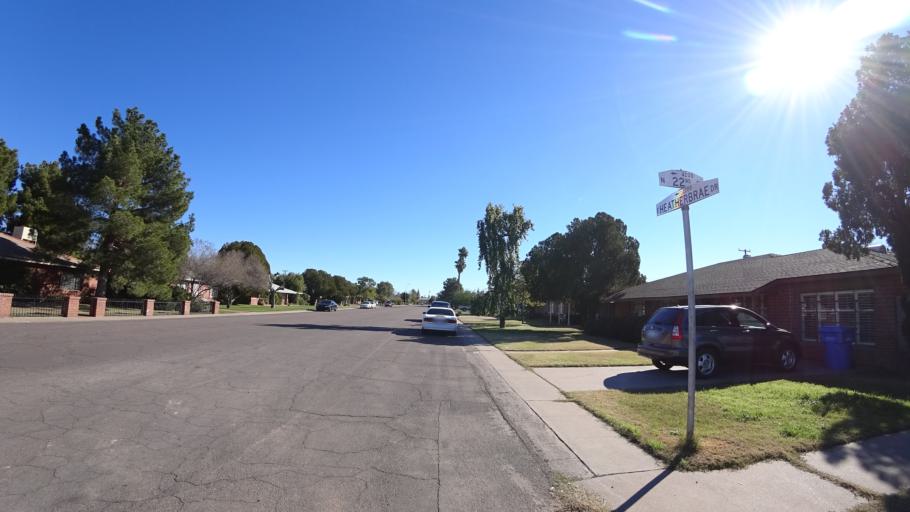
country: US
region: Arizona
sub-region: Maricopa County
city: Phoenix
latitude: 33.4974
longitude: -112.0345
